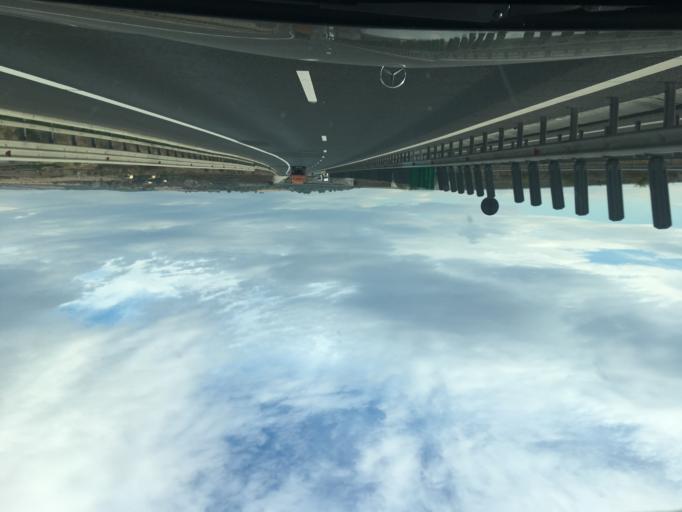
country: RO
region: Sibiu
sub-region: Comuna Orlat
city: Orlat
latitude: 45.7831
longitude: 23.9491
